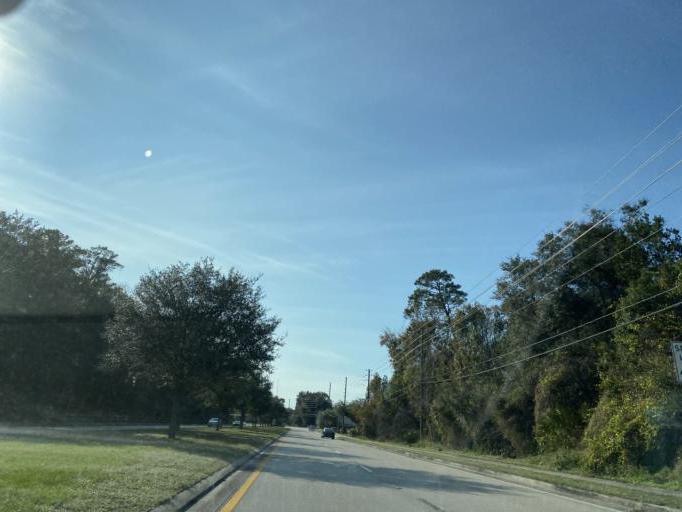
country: US
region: Florida
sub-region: Seminole County
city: Longwood
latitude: 28.7269
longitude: -81.3291
